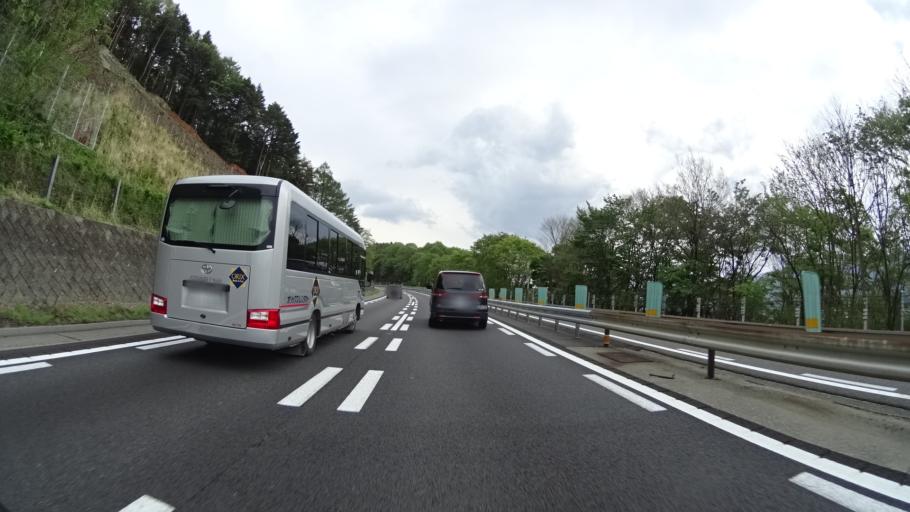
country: JP
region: Nagano
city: Tatsuno
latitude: 35.9882
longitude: 138.0061
